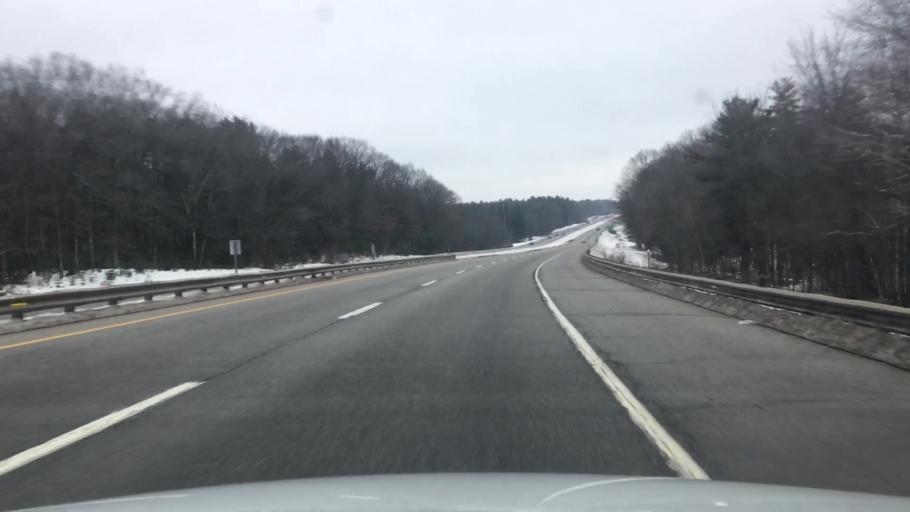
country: US
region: Maine
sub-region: Cumberland County
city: Scarborough
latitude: 43.6060
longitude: -70.3192
